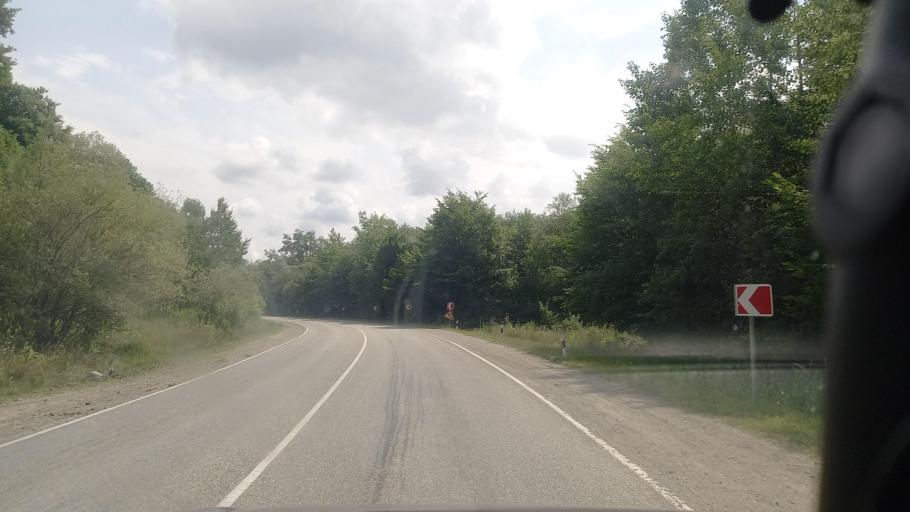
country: RU
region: Karachayevo-Cherkesiya
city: Kurdzhinovo
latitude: 44.0380
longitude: 40.9091
